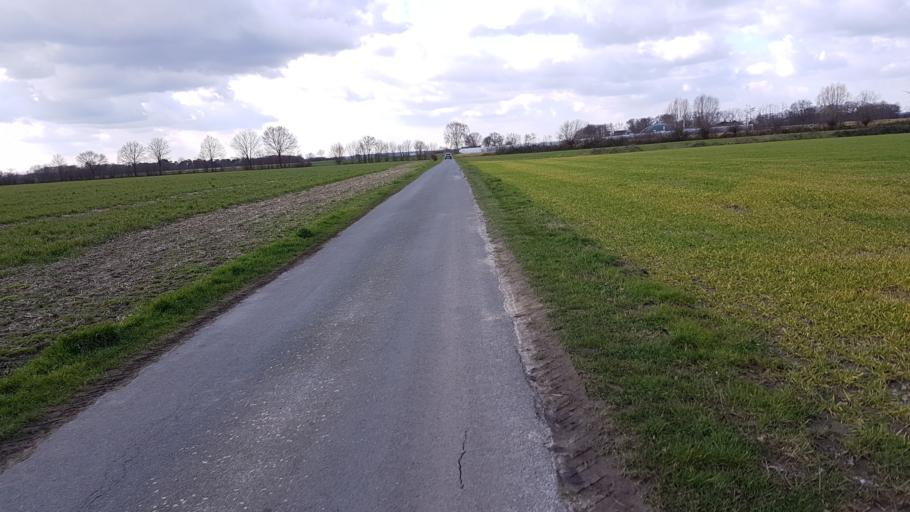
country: DE
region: North Rhine-Westphalia
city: Olfen
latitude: 51.6949
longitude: 7.3767
